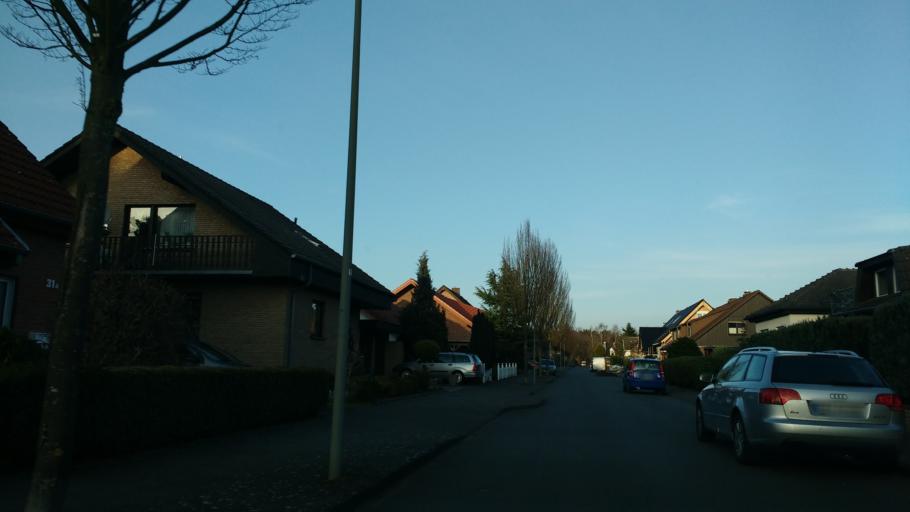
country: DE
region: North Rhine-Westphalia
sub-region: Regierungsbezirk Detmold
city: Hovelhof
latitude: 51.7840
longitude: 8.7145
